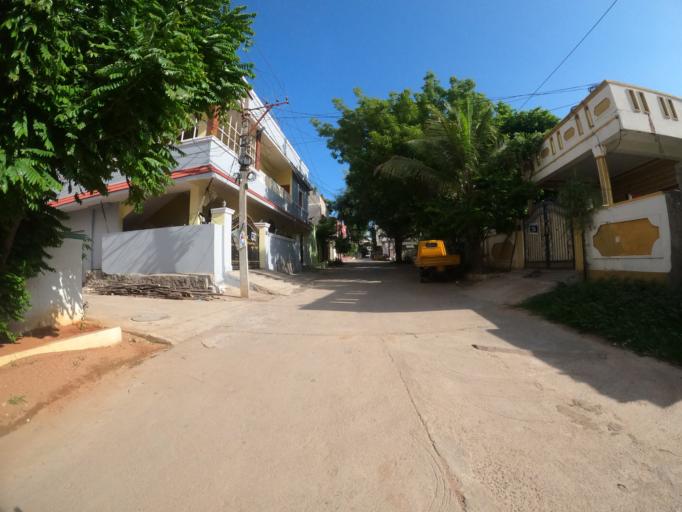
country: IN
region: Telangana
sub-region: Hyderabad
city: Hyderabad
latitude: 17.3588
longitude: 78.3791
